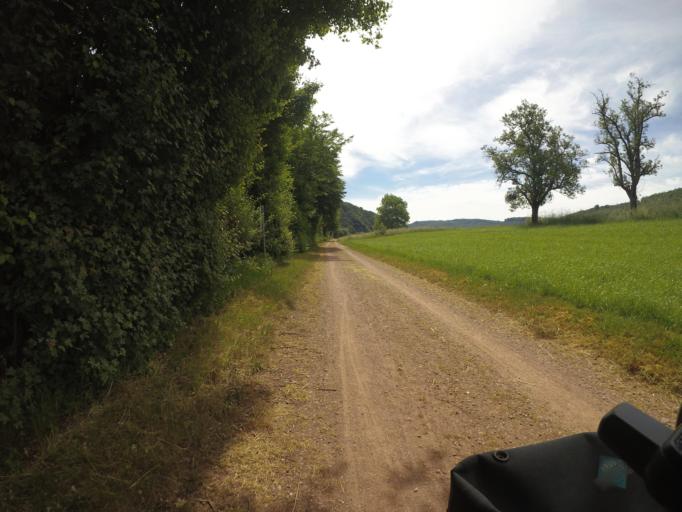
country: DE
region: Rheinland-Pfalz
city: Serrig
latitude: 49.5914
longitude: 6.5627
